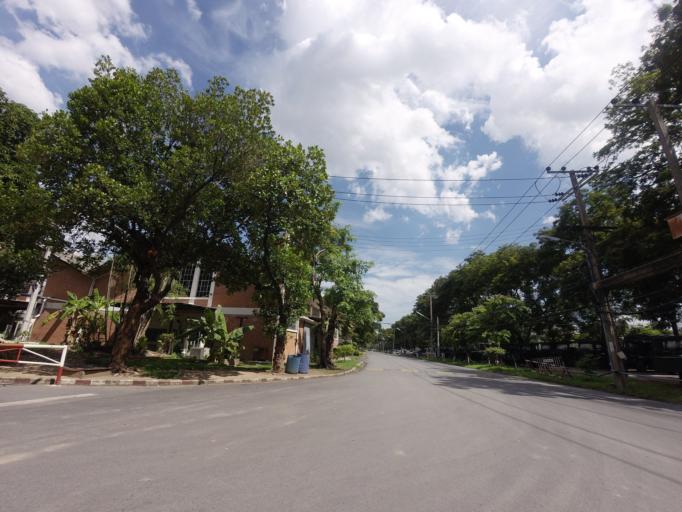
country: TH
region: Bangkok
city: Khlong Toei
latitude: 13.7295
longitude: 100.5526
